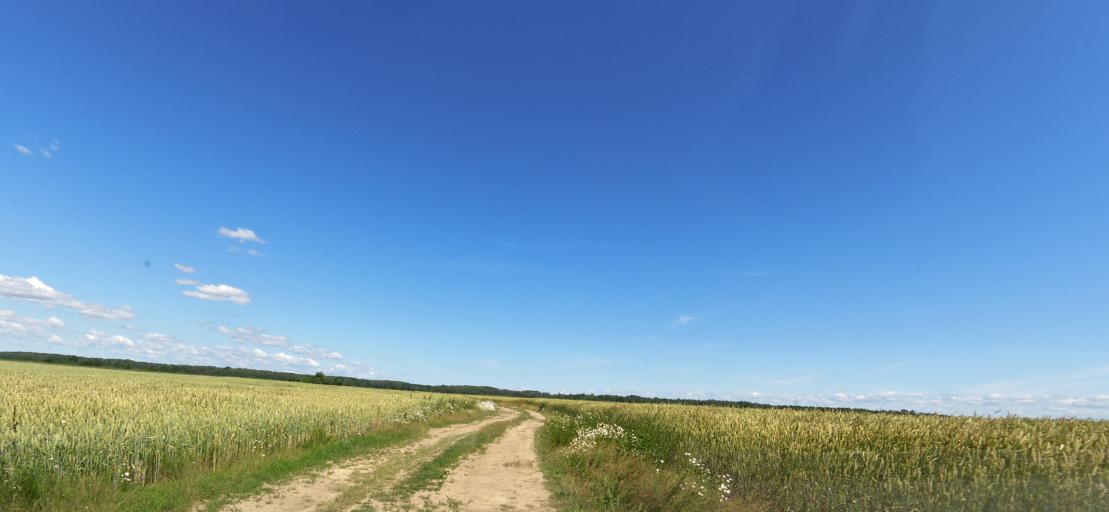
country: LT
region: Panevezys
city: Pasvalys
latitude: 56.2672
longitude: 24.5131
